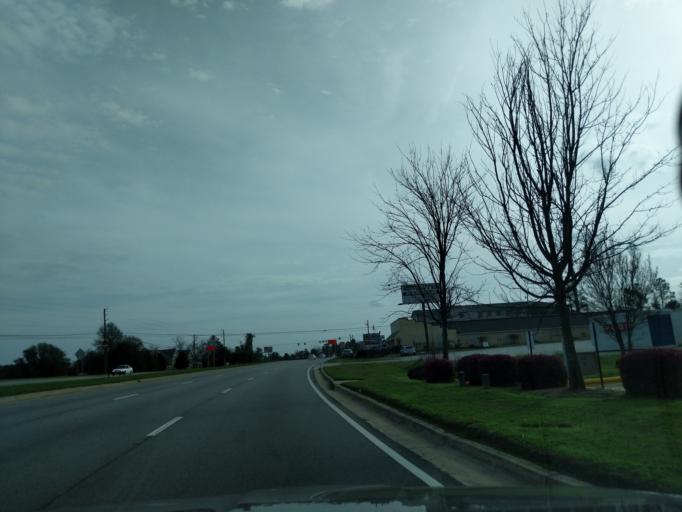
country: US
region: Georgia
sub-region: Columbia County
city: Evans
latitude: 33.4781
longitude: -82.1294
